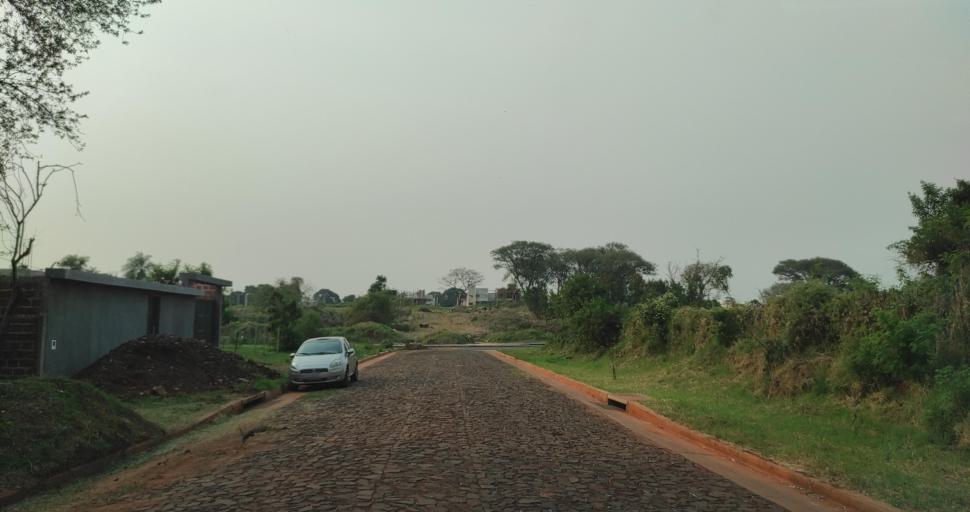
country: AR
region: Misiones
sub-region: Departamento de Capital
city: Posadas
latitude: -27.3956
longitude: -55.9271
